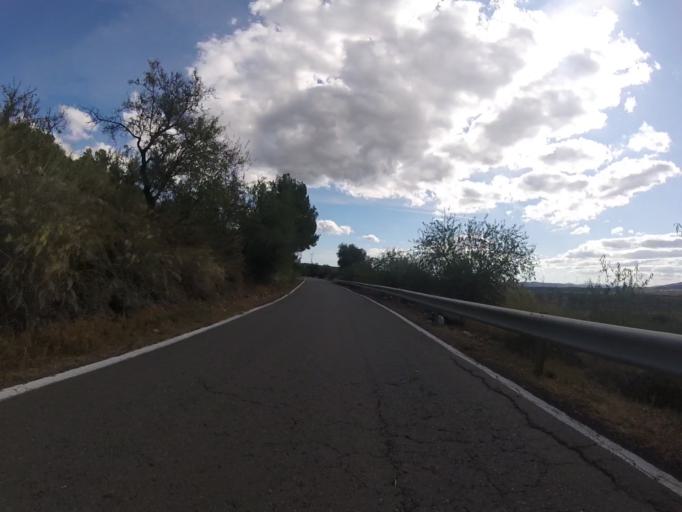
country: ES
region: Valencia
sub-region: Provincia de Castello
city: Cuevas de Vinroma
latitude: 40.3648
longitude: 0.1214
